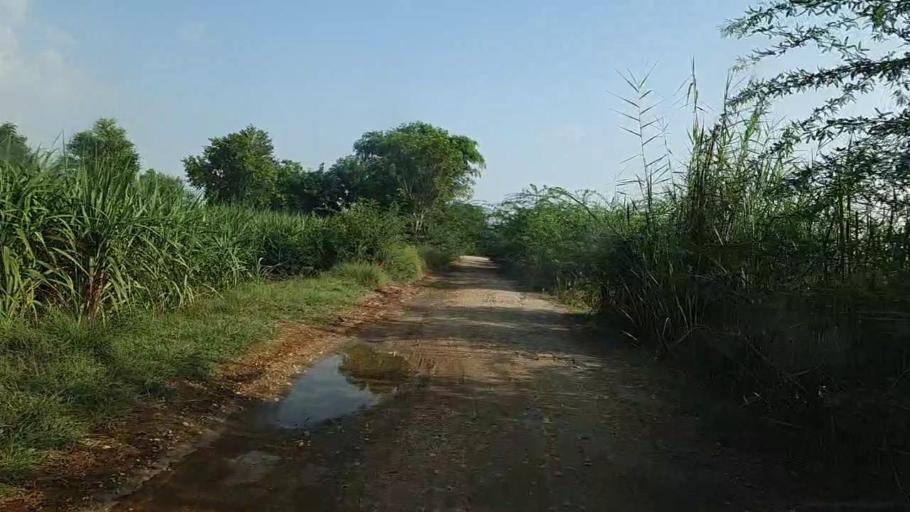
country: PK
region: Sindh
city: Pad Idan
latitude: 26.8338
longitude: 68.2413
